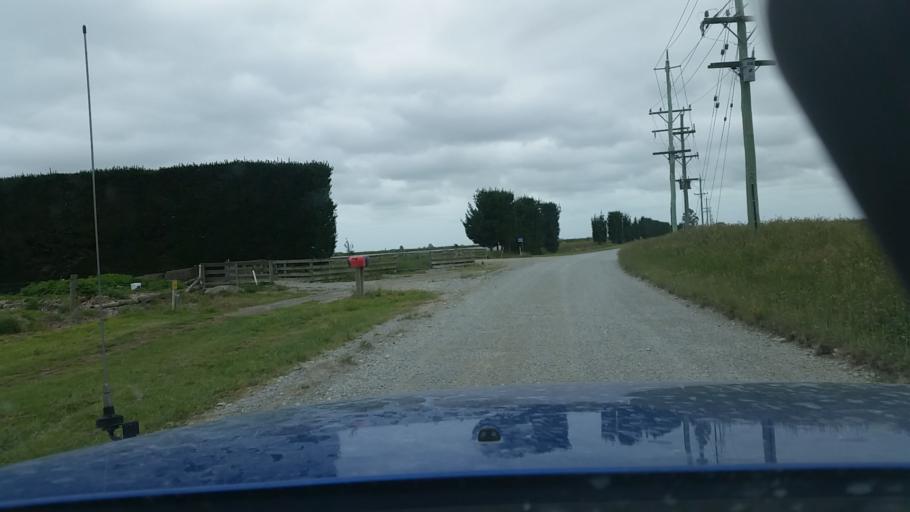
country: NZ
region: Canterbury
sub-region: Ashburton District
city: Tinwald
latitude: -44.0262
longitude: 171.5314
